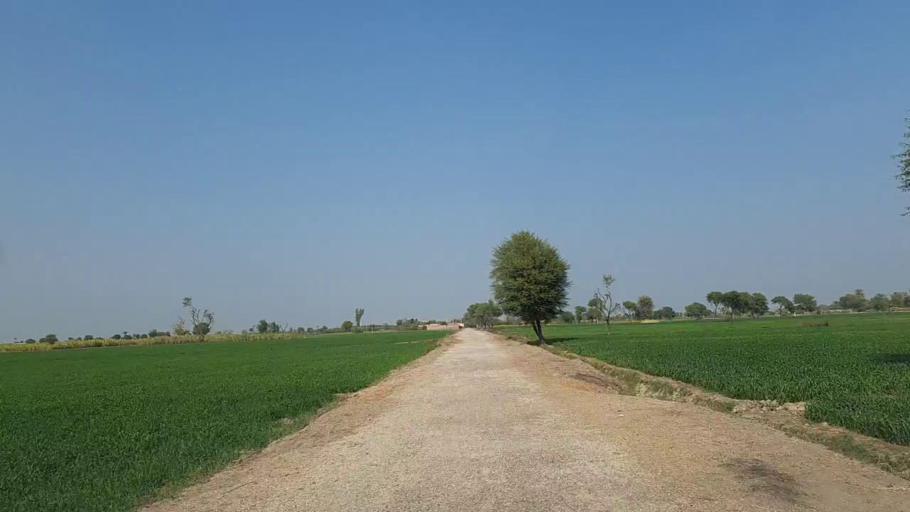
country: PK
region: Sindh
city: Jam Sahib
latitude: 26.2691
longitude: 68.5210
